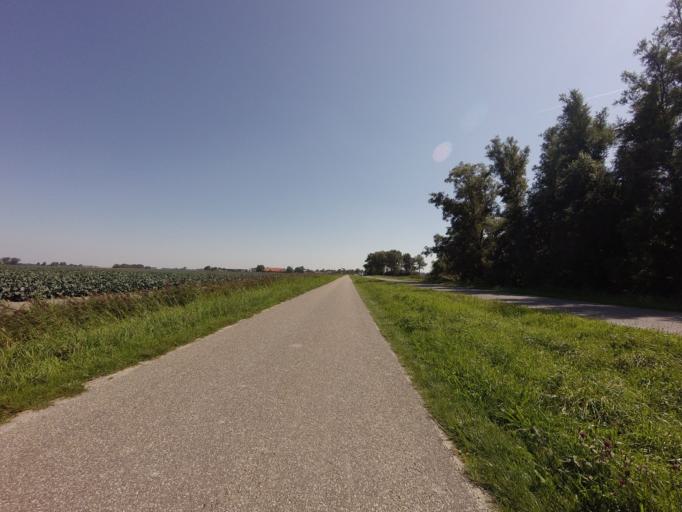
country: NL
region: Friesland
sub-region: Gemeente Dongeradeel
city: Ternaard
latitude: 53.3813
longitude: 6.0353
